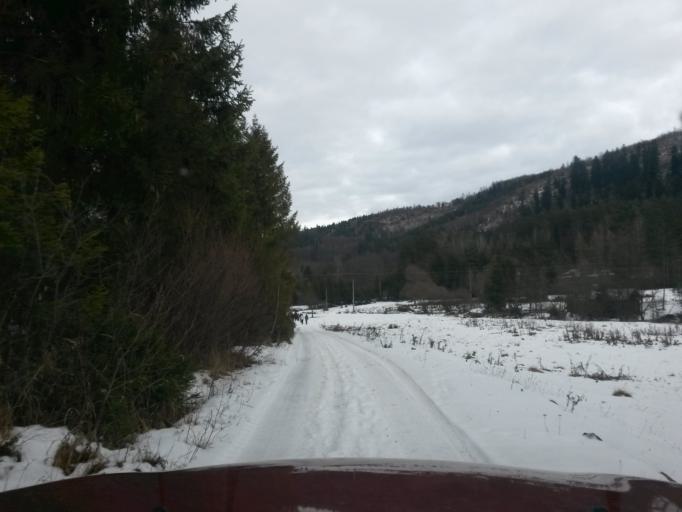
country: SK
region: Kosicky
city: Spisska Nova Ves
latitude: 48.8829
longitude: 20.5936
